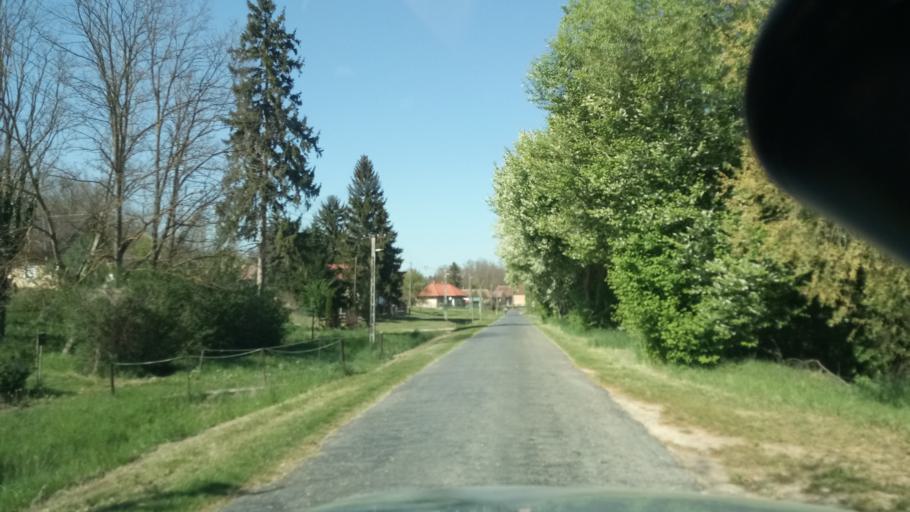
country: HU
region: Zala
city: Sarmellek
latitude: 46.6991
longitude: 17.1034
